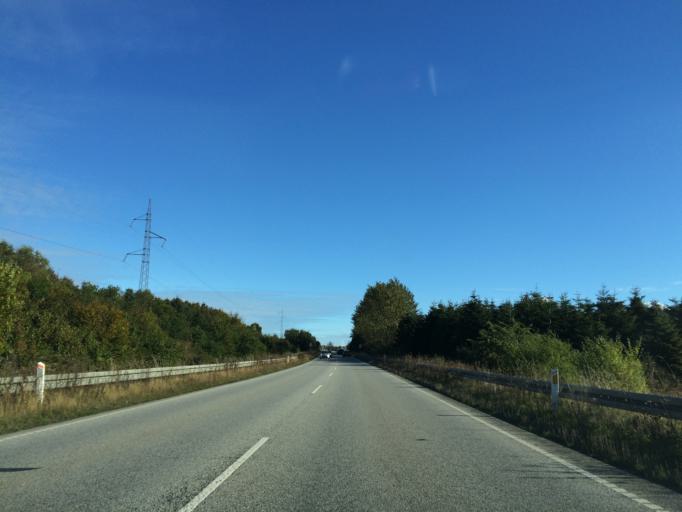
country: DK
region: Central Jutland
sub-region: Randers Kommune
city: Randers
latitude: 56.4363
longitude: 10.0653
